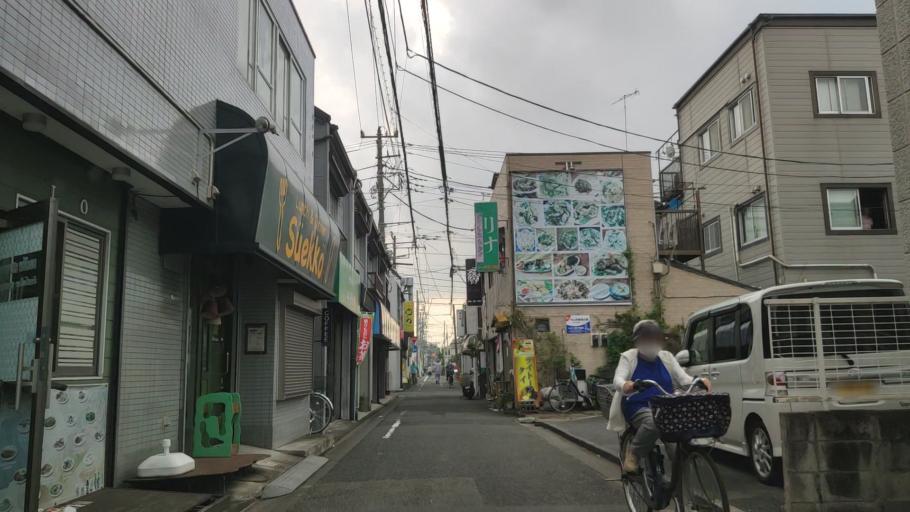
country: JP
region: Kanagawa
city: Minami-rinkan
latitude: 35.4900
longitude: 139.4498
